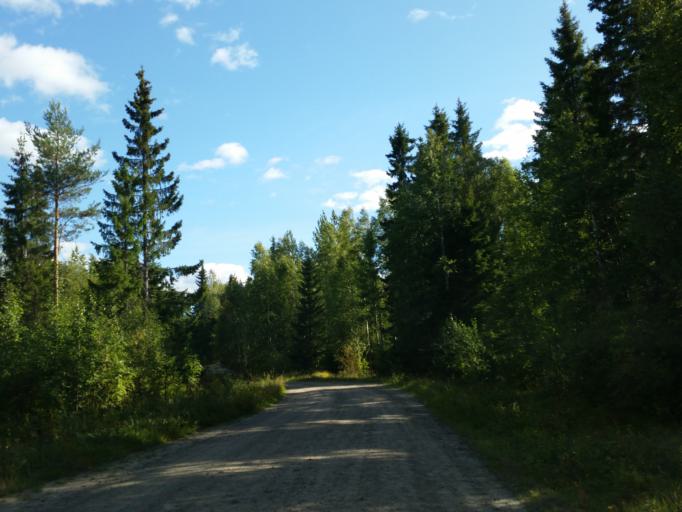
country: SE
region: Vaesterbotten
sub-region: Robertsfors Kommun
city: Robertsfors
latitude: 64.1623
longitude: 20.9532
